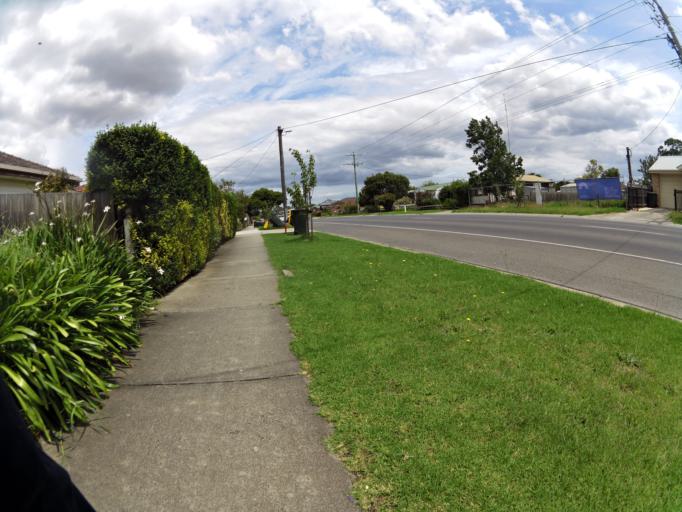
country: AU
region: Victoria
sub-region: Latrobe
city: Traralgon
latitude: -38.1891
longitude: 146.5343
